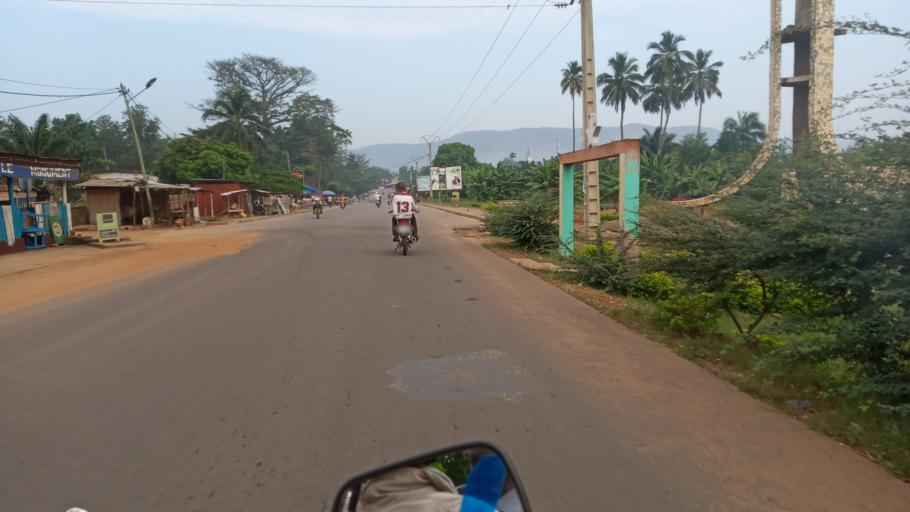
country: TG
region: Plateaux
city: Kpalime
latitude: 6.9016
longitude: 0.6339
